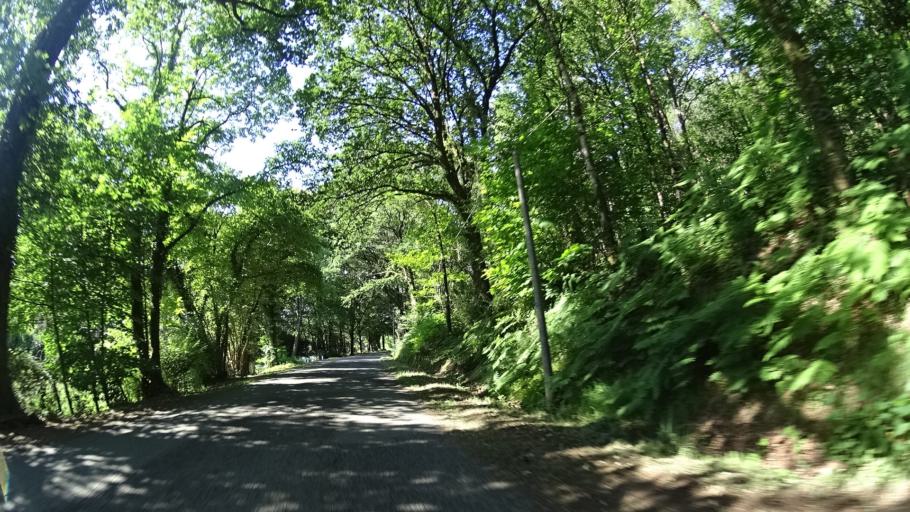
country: FR
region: Brittany
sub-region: Departement d'Ille-et-Vilaine
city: Guipry
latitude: 47.7769
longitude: -1.8434
